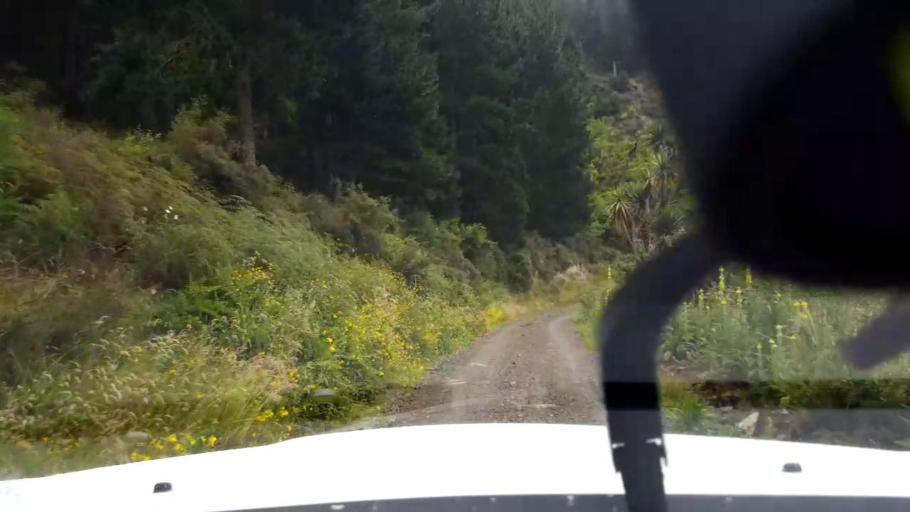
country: NZ
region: Canterbury
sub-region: Timaru District
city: Pleasant Point
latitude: -44.0337
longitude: 170.9995
